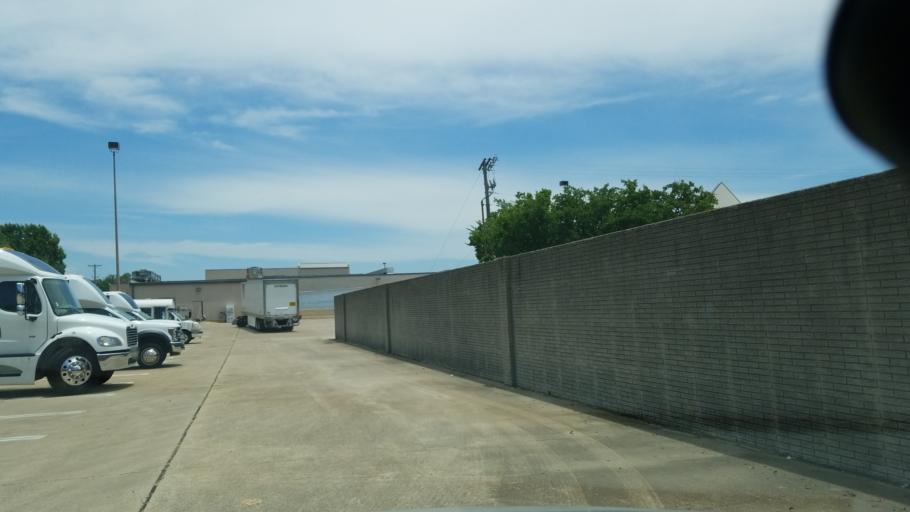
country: US
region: Texas
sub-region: Dallas County
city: Irving
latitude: 32.8385
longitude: -96.9624
